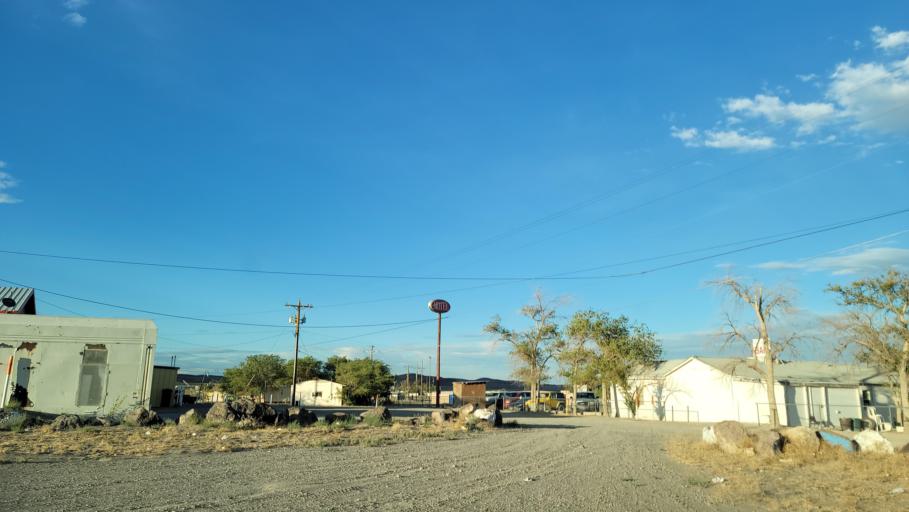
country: US
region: Nevada
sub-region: Lyon County
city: Silver Springs
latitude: 39.4157
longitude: -119.2237
